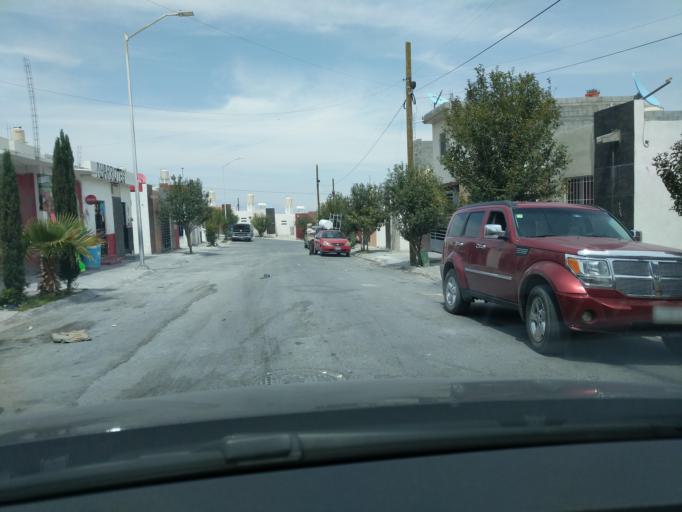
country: MX
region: Coahuila
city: Saltillo
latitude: 25.3468
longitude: -101.0065
